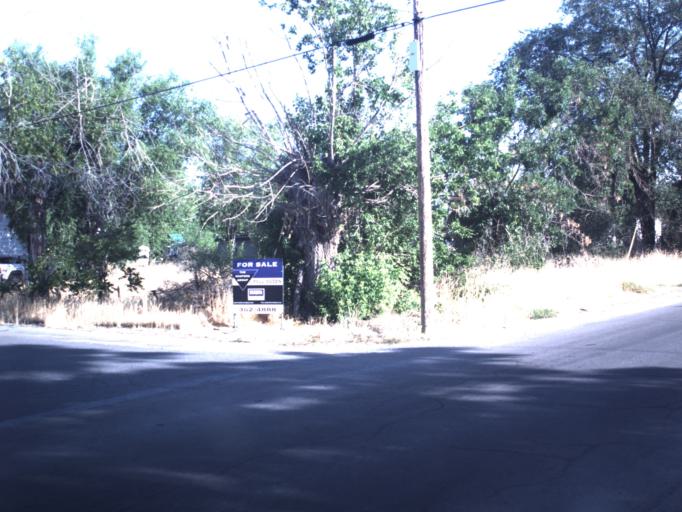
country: US
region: Utah
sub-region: Utah County
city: American Fork
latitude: 40.3757
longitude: -111.7854
